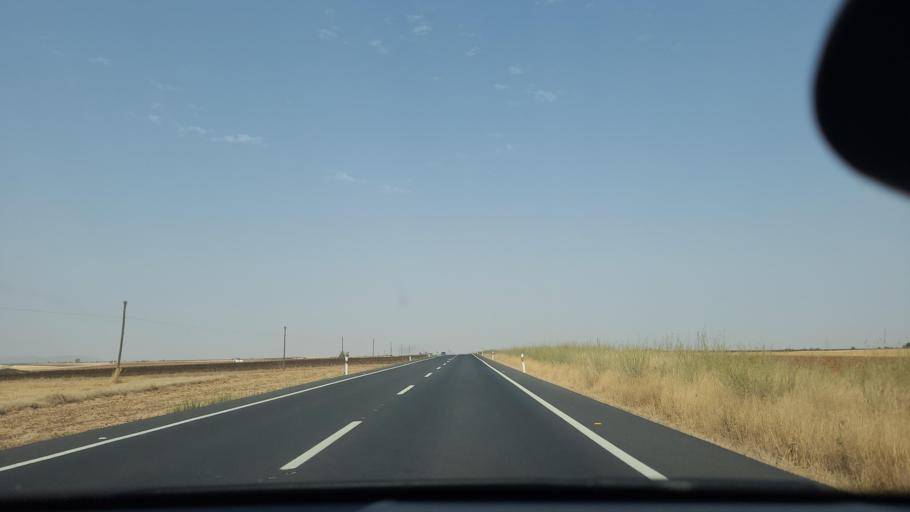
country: ES
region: Extremadura
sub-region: Provincia de Badajoz
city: Azuaga
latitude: 38.2635
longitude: -5.7366
